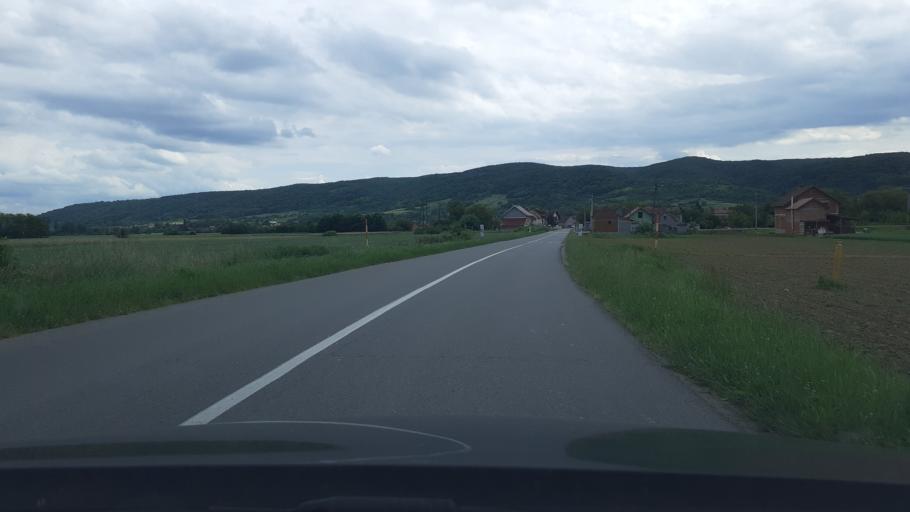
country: HR
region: Pozesko-Slavonska
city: Jaksic
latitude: 45.3374
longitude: 17.7594
